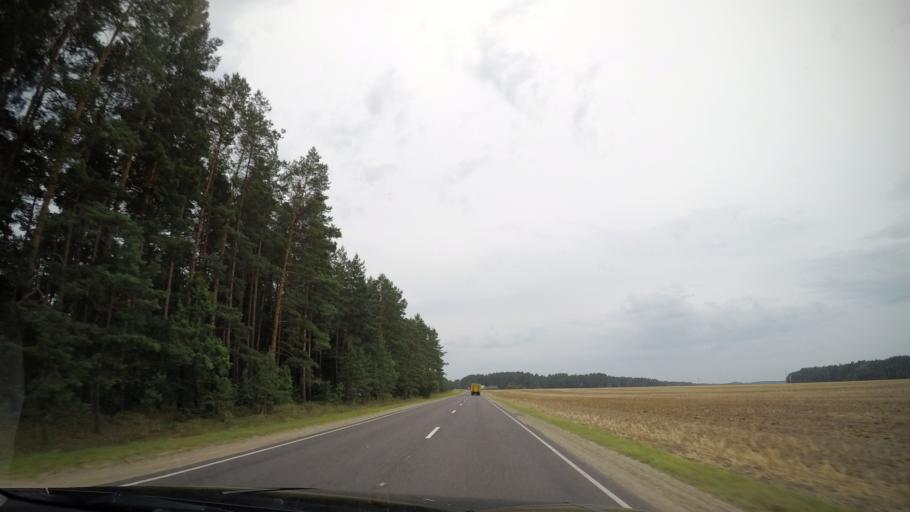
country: BY
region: Grodnenskaya
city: Iwye
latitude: 53.9014
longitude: 25.7533
